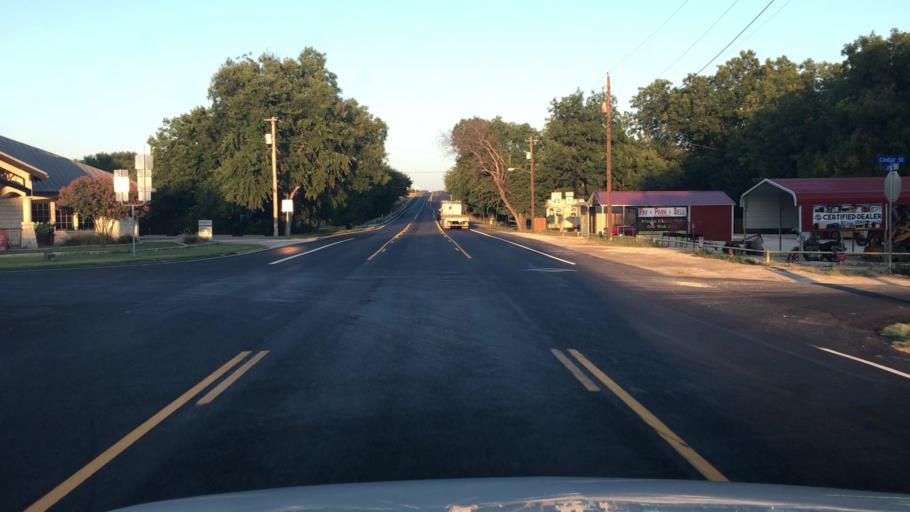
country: US
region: Texas
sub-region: Hamilton County
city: Hico
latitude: 31.9820
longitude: -98.0287
